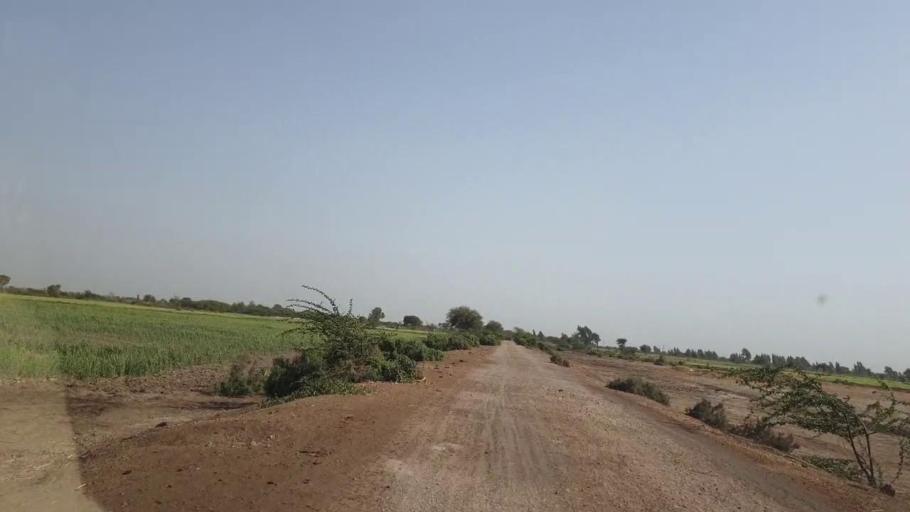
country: PK
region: Sindh
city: Rajo Khanani
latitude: 25.0406
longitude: 68.8505
